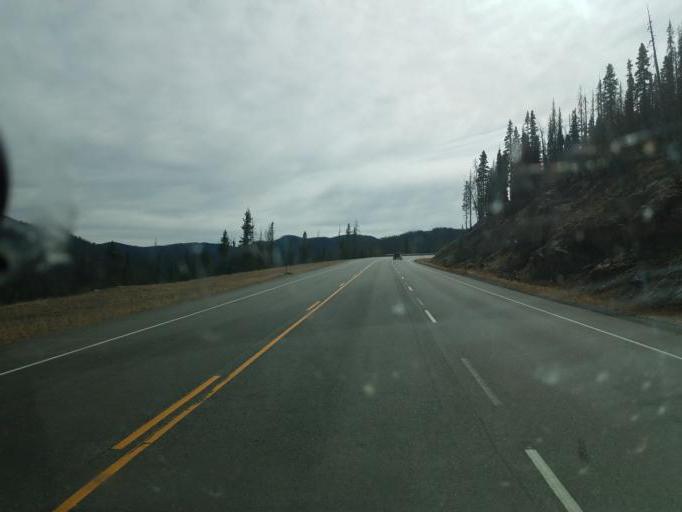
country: US
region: Colorado
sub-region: Archuleta County
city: Pagosa Springs
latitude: 37.4942
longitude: -106.7670
